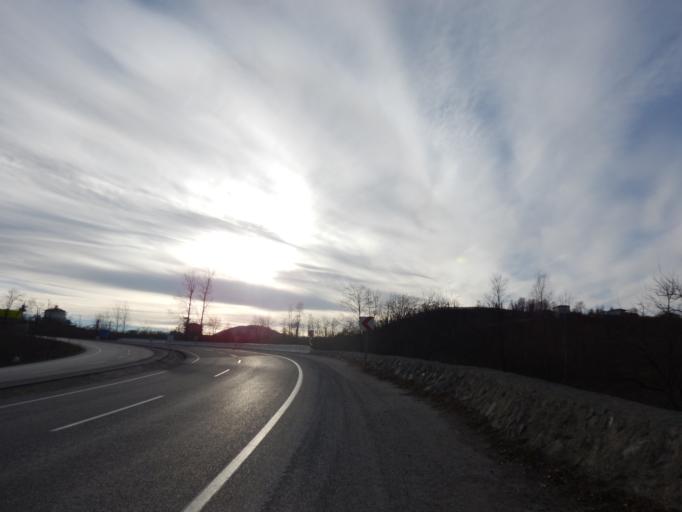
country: TR
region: Ordu
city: Uzunisa
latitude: 40.9025
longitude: 37.8257
